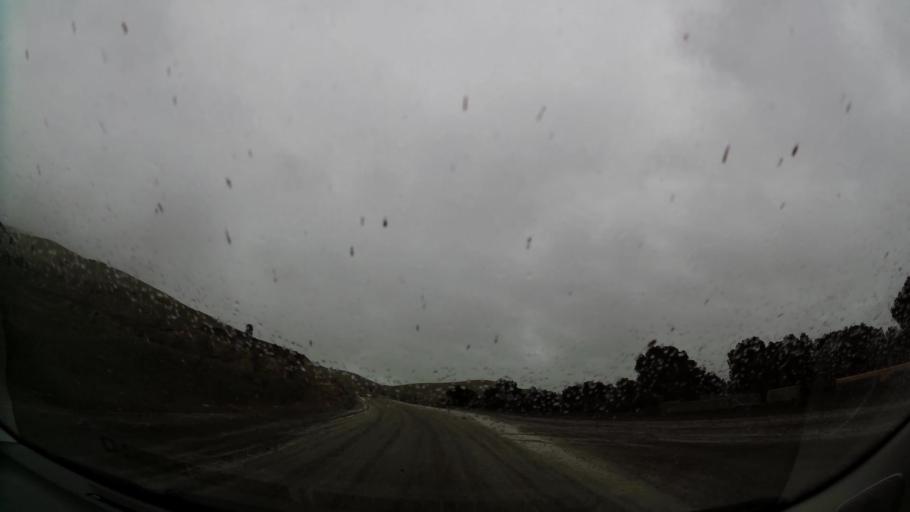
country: MA
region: Taza-Al Hoceima-Taounate
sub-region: Taza
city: Ajdir
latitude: 34.9020
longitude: -3.7903
